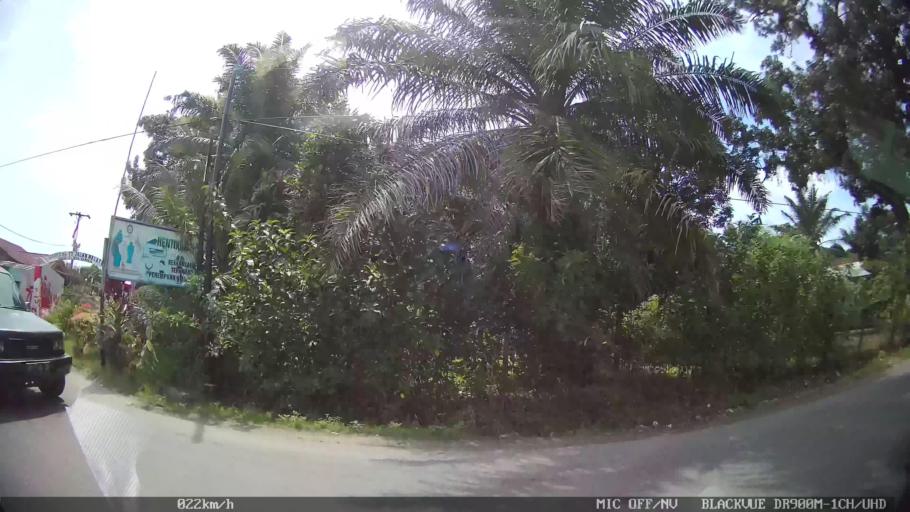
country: ID
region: North Sumatra
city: Medan
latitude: 3.6287
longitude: 98.7154
